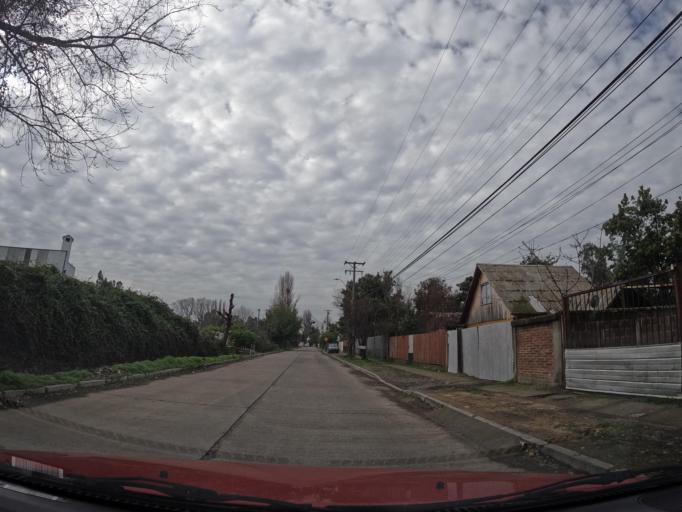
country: CL
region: Maule
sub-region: Provincia de Linares
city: Linares
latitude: -35.8540
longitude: -71.6121
